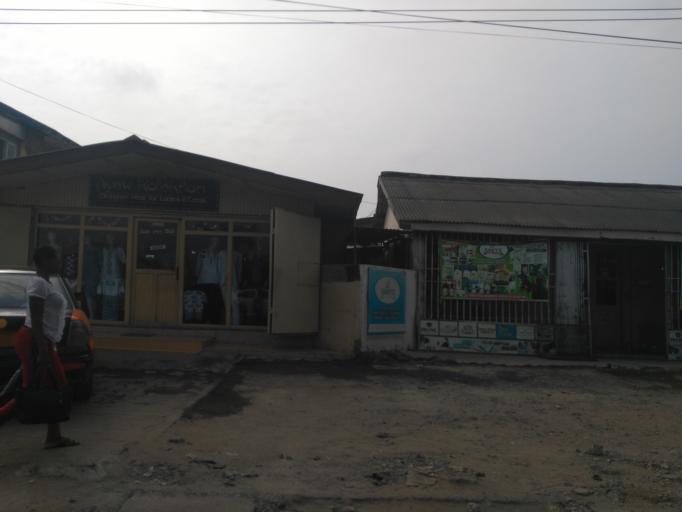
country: GH
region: Greater Accra
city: Accra
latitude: 5.5529
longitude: -0.1765
